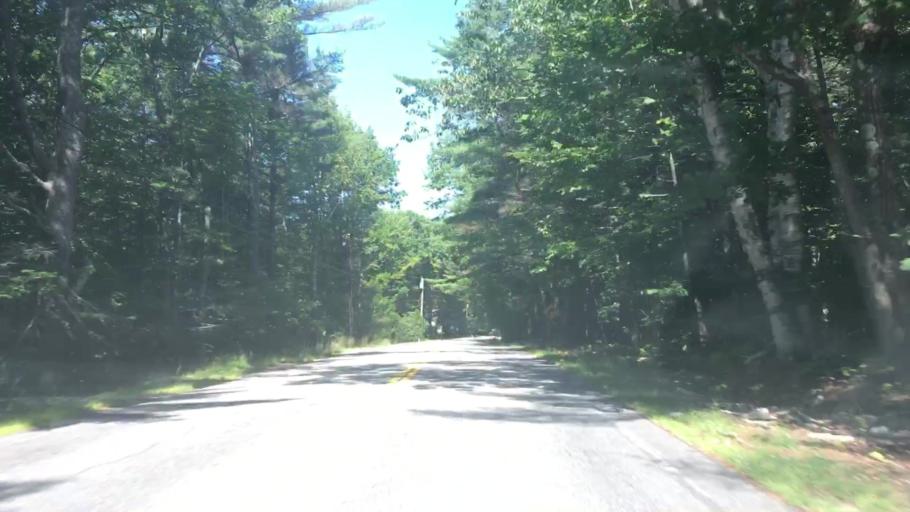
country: US
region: Maine
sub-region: Androscoggin County
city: Lisbon
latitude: 44.0592
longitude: -70.1181
